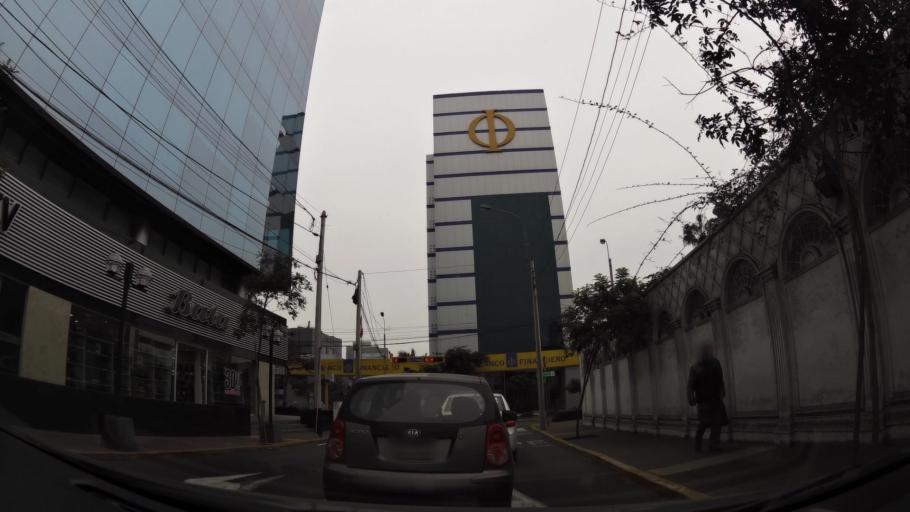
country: PE
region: Lima
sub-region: Lima
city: San Isidro
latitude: -12.1188
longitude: -77.0274
